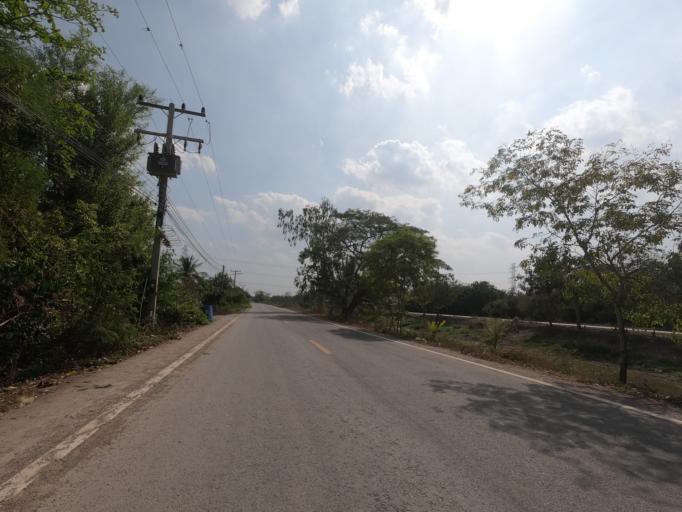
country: TH
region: Pathum Thani
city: Nong Suea
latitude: 14.2139
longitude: 100.8462
